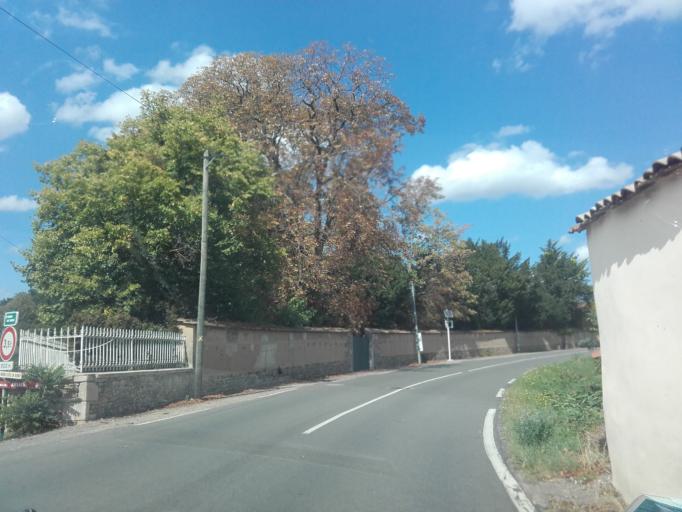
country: FR
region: Bourgogne
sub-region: Departement de Saone-et-Loire
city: La Chapelle-de-Guinchay
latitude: 46.2149
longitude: 4.7563
